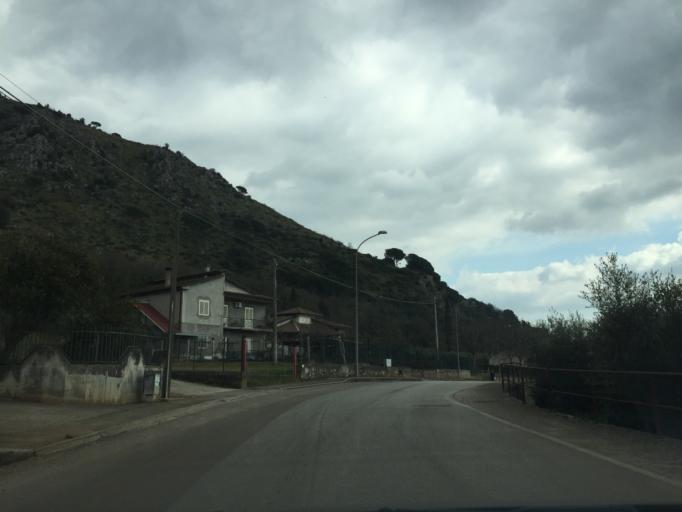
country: IT
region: Latium
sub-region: Provincia di Frosinone
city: Villa Santa Lucia
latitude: 41.4934
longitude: 13.7802
